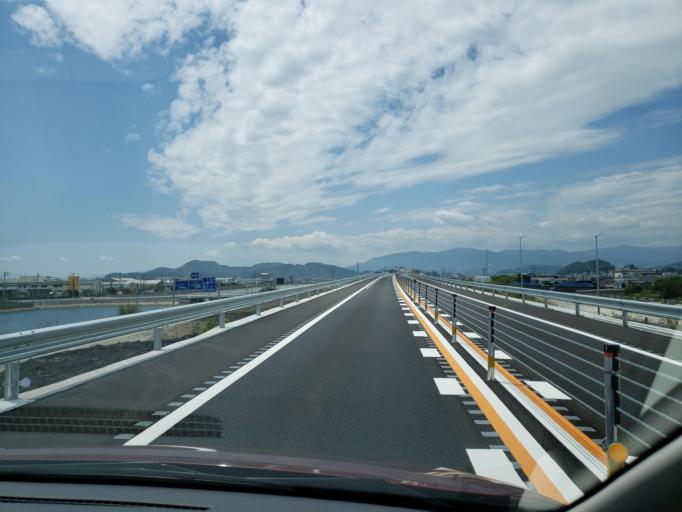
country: JP
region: Tokushima
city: Tokushima-shi
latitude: 34.0660
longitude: 134.5949
